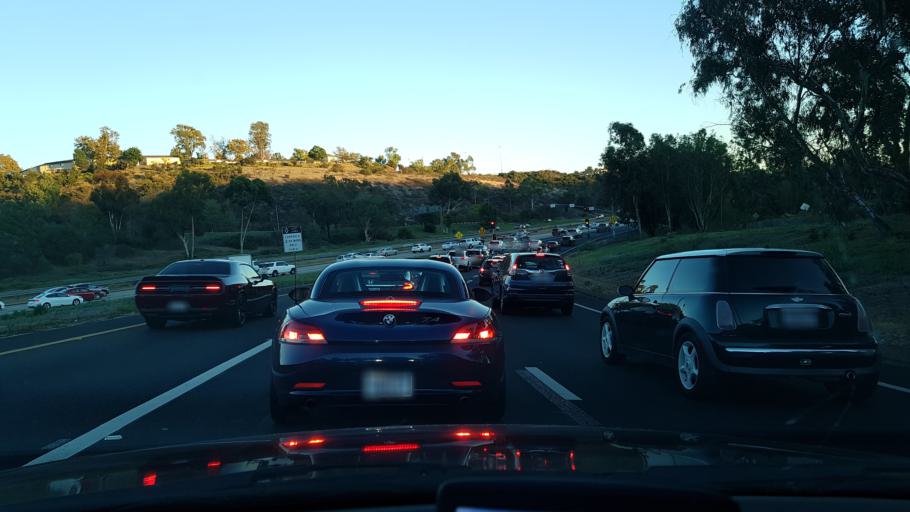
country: US
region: California
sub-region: San Diego County
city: La Mesa
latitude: 32.8218
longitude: -117.1172
